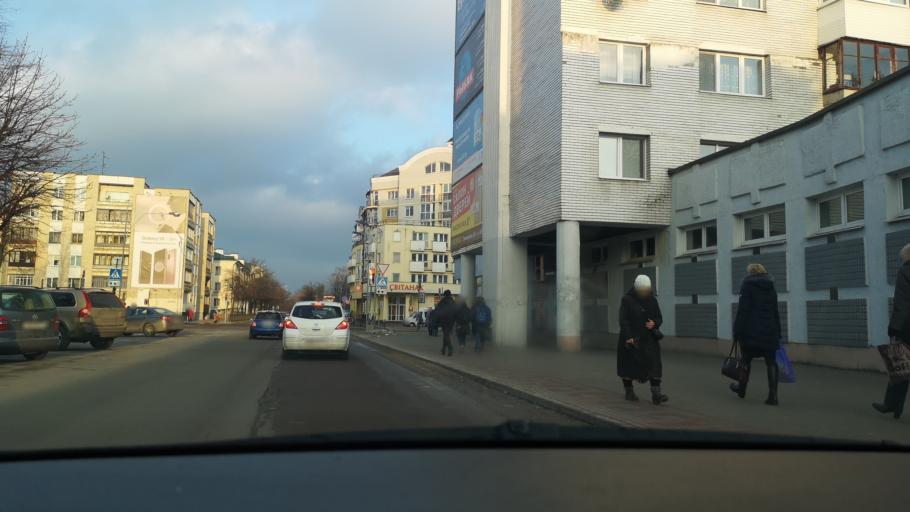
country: BY
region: Brest
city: Brest
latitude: 52.0974
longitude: 23.6949
